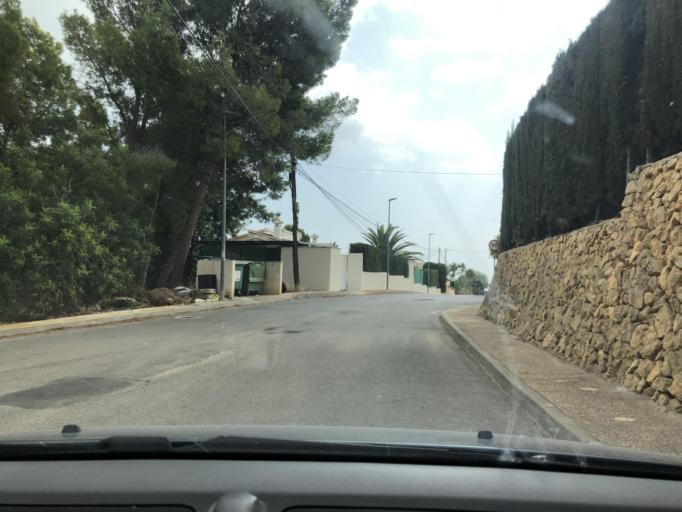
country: ES
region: Valencia
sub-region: Provincia de Alicante
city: Altea
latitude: 38.6394
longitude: -0.0676
